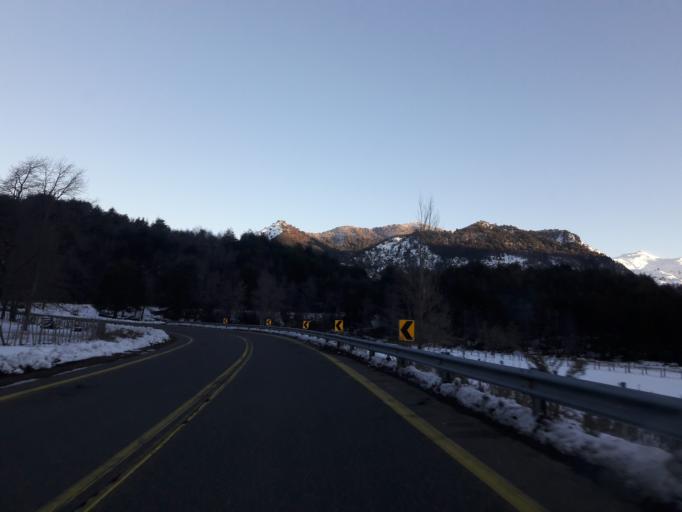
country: CL
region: Araucania
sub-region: Provincia de Cautin
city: Vilcun
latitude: -38.5020
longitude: -71.5204
